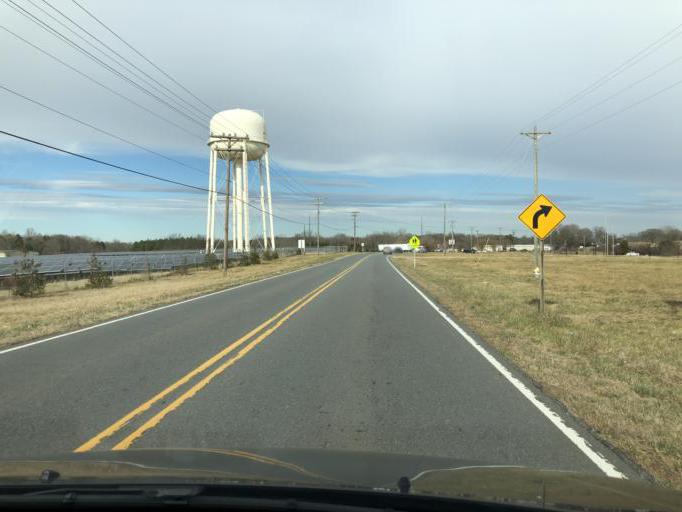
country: US
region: North Carolina
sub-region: Cleveland County
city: Shelby
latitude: 35.2569
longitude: -81.5048
